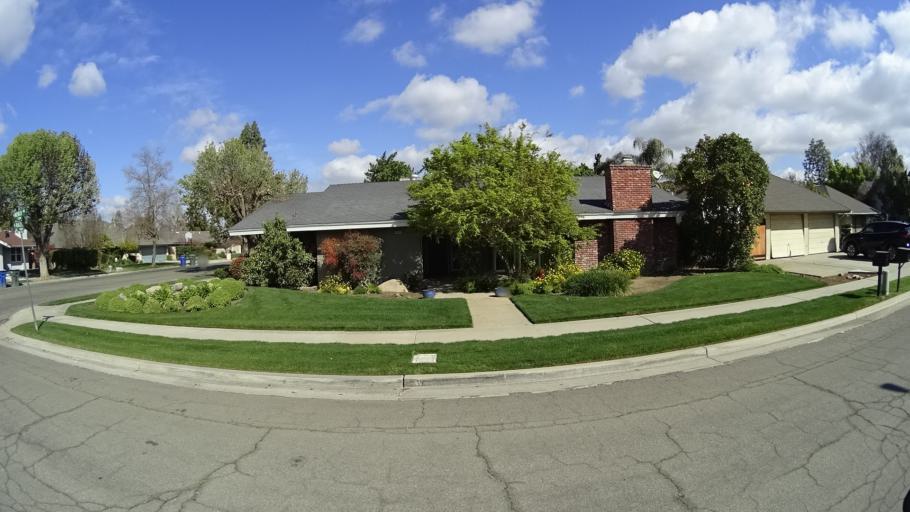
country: US
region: California
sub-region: Fresno County
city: Fresno
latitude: 36.8308
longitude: -119.8501
